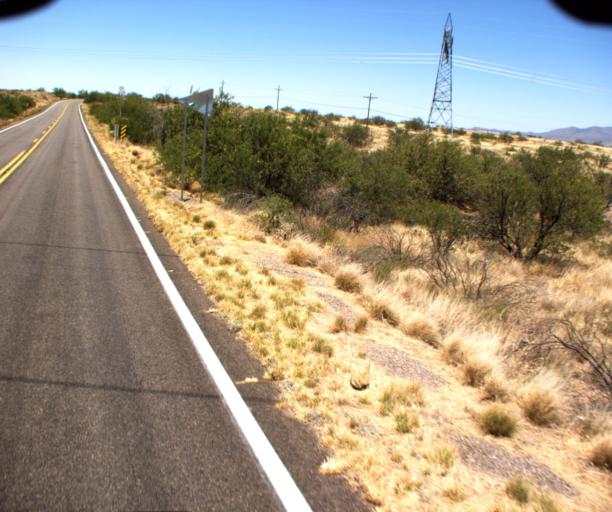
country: US
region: Arizona
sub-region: Pima County
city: Catalina
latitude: 32.6034
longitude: -110.9827
